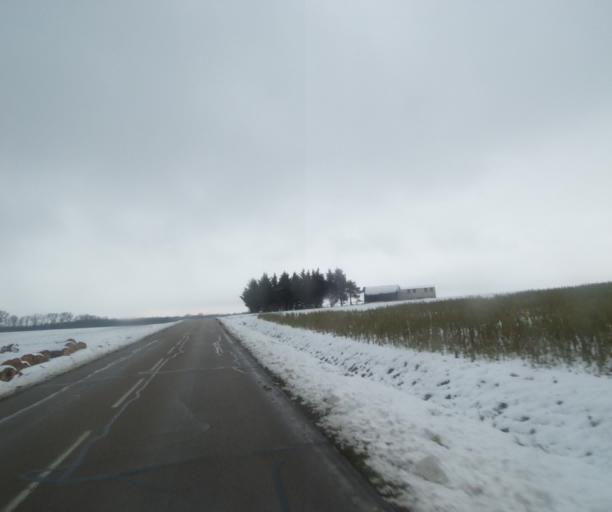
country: FR
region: Champagne-Ardenne
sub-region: Departement de la Haute-Marne
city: Laneuville-a-Remy
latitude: 48.4361
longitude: 4.8561
